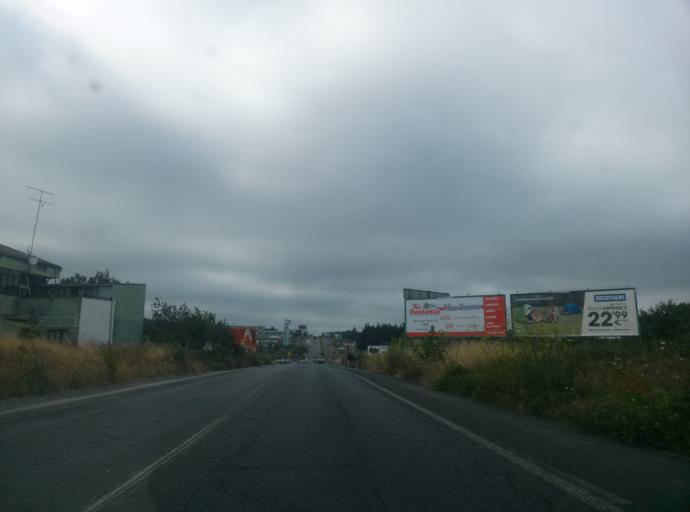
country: ES
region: Galicia
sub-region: Provincia de Lugo
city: Lugo
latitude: 43.0334
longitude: -7.5640
